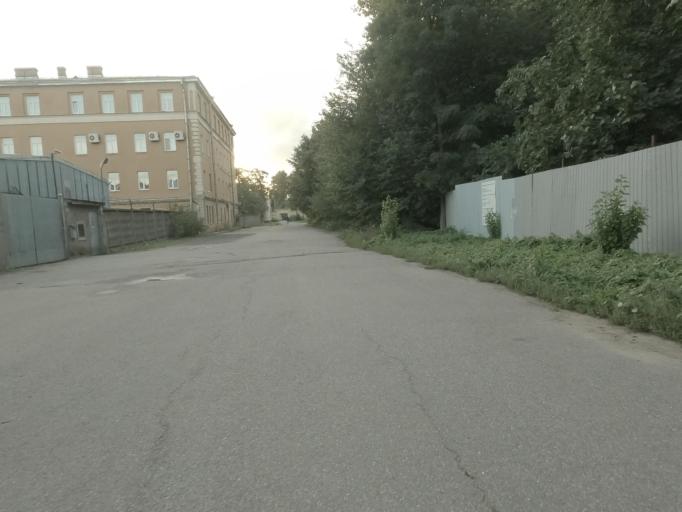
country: RU
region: St.-Petersburg
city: Admiralteisky
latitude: 59.8990
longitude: 30.2592
